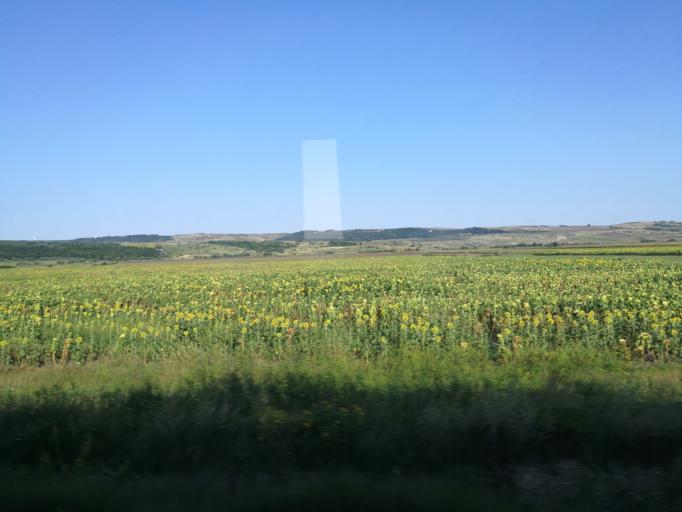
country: RO
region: Vaslui
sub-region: Comuna Albesti
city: Albesti
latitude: 46.4873
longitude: 27.8190
